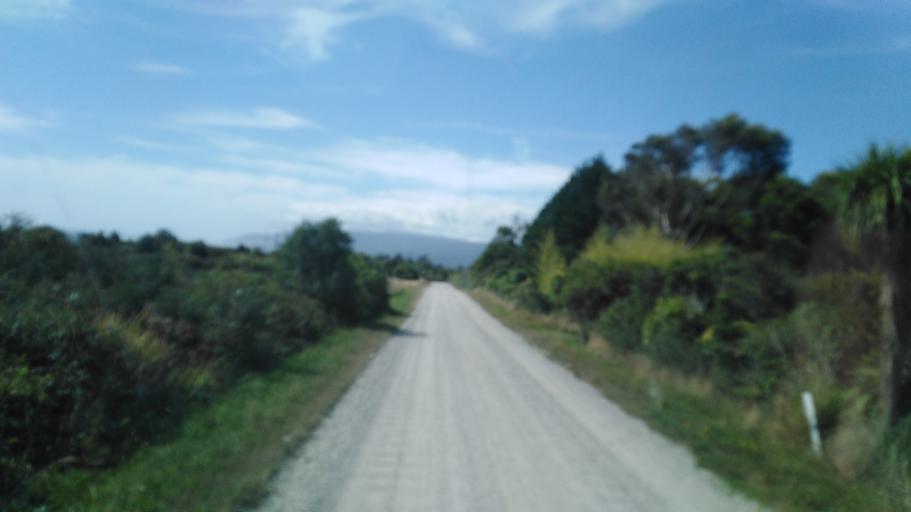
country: NZ
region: West Coast
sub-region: Buller District
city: Westport
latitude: -41.2640
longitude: 172.1139
